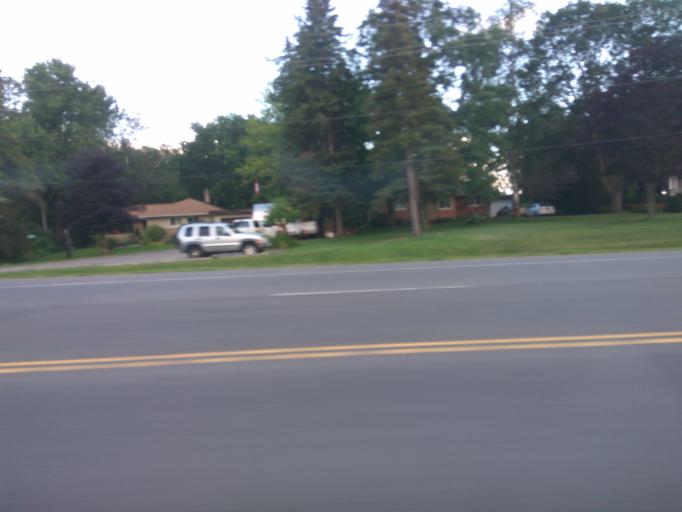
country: CA
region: Ontario
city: Stratford
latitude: 43.3701
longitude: -80.9219
